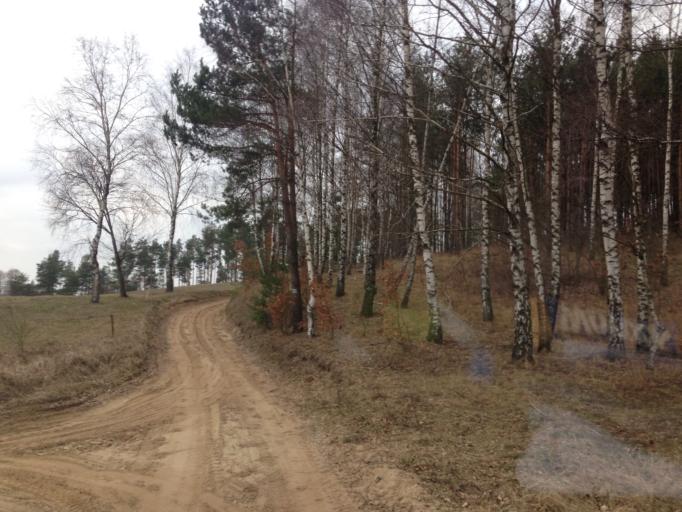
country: PL
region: Warmian-Masurian Voivodeship
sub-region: Powiat dzialdowski
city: Lidzbark
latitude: 53.3757
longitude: 19.7658
